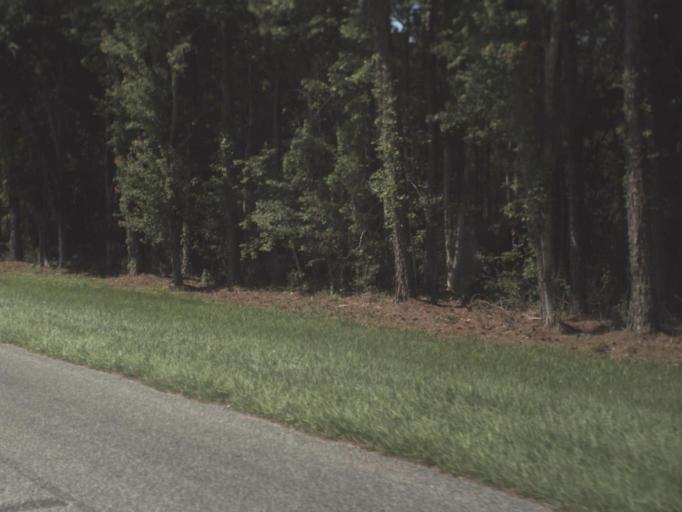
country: US
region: Florida
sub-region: Saint Johns County
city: Villano Beach
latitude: 29.9975
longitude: -81.4689
